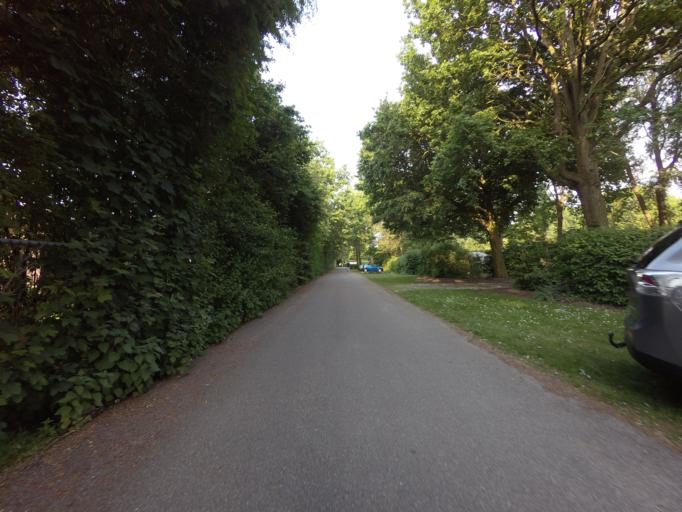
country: NL
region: South Holland
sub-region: Gemeente Lansingerland
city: Bleiswijk
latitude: 52.0092
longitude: 4.5615
